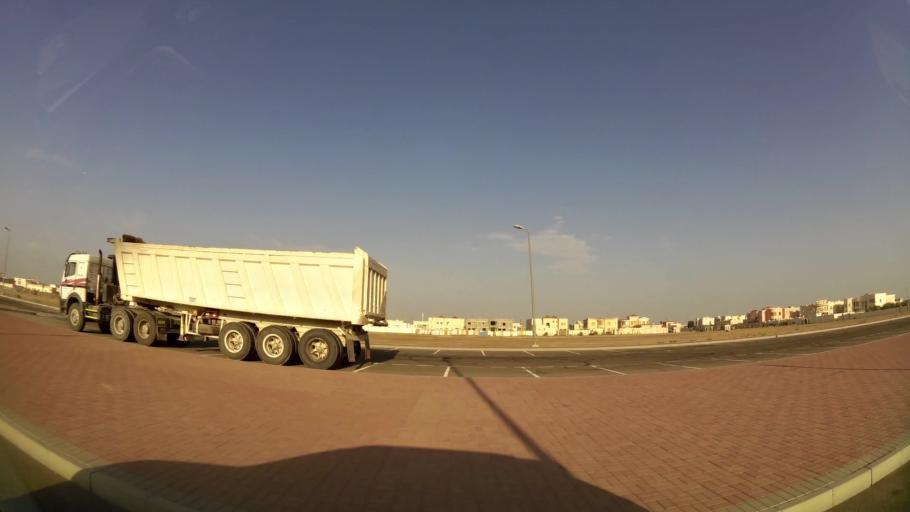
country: AE
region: Abu Dhabi
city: Al Ain
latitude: 24.0985
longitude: 55.8355
